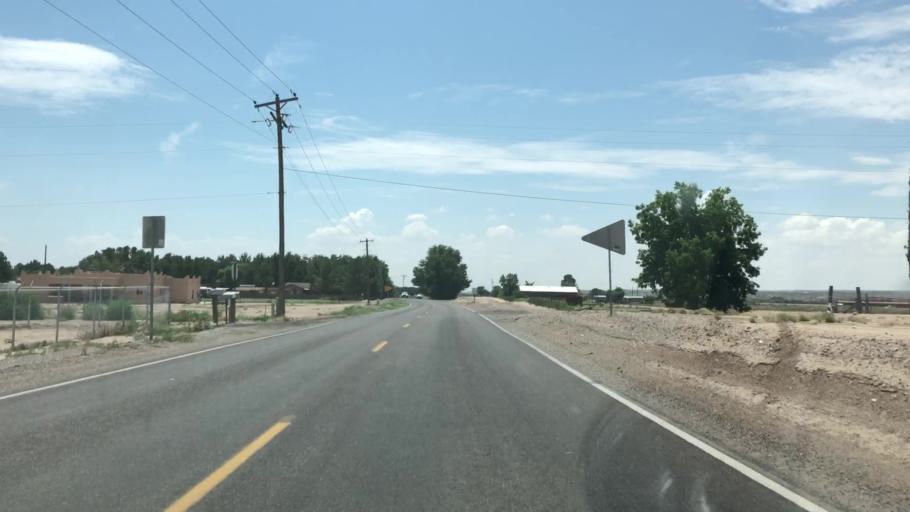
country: US
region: New Mexico
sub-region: Dona Ana County
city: Vado
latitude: 32.0866
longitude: -106.6834
